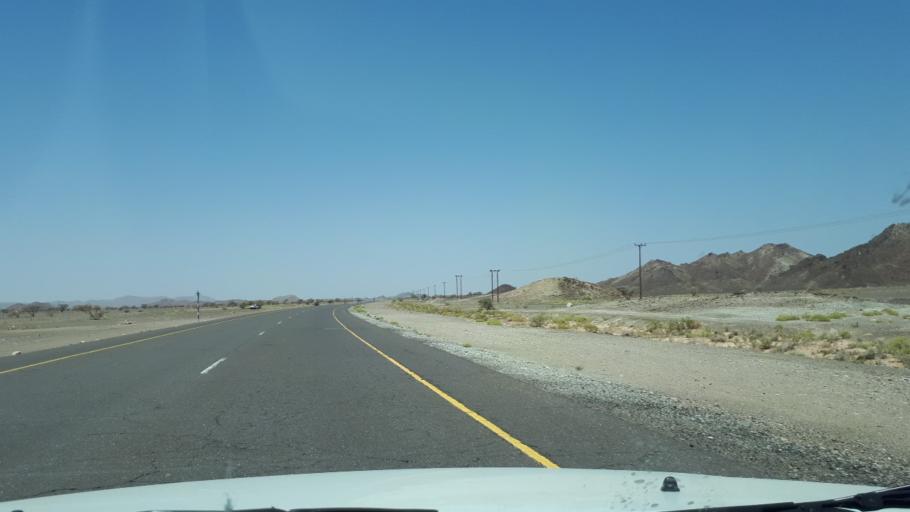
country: OM
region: Ash Sharqiyah
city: Ibra'
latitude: 22.6184
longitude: 58.4390
